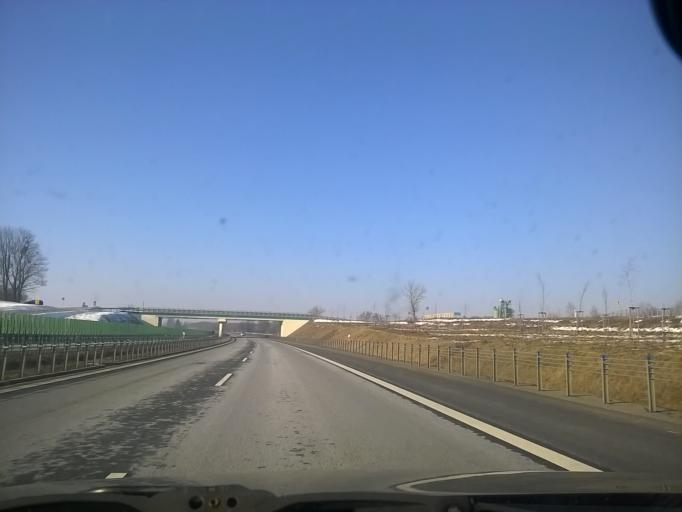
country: PL
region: Warmian-Masurian Voivodeship
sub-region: Powiat olsztynski
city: Biskupiec
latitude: 53.8381
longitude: 21.0190
